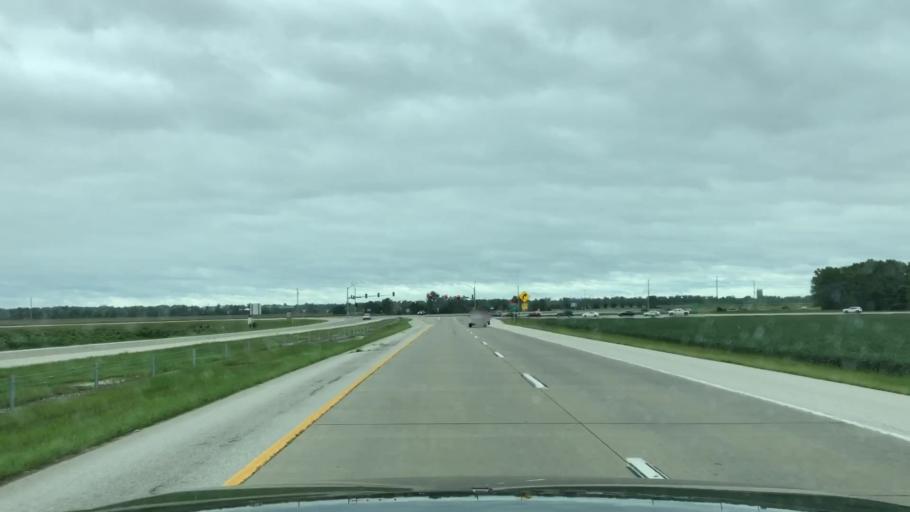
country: US
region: Missouri
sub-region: Saint Charles County
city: Saint Charles
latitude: 38.7227
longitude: -90.4982
